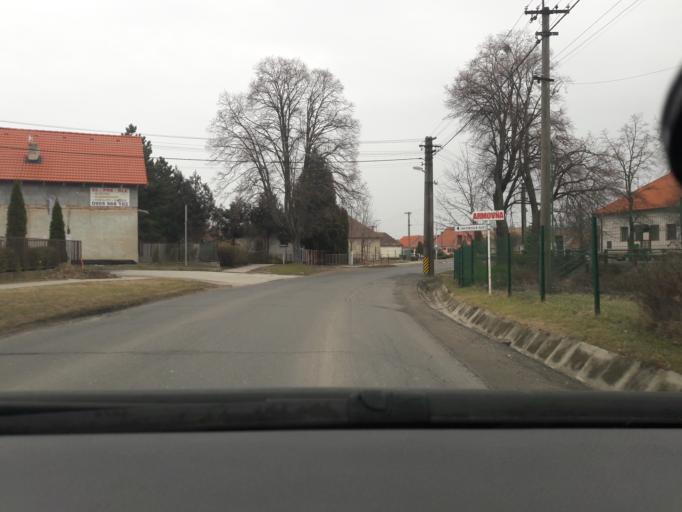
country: SK
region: Bratislavsky
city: Senec
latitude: 48.2966
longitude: 17.4537
